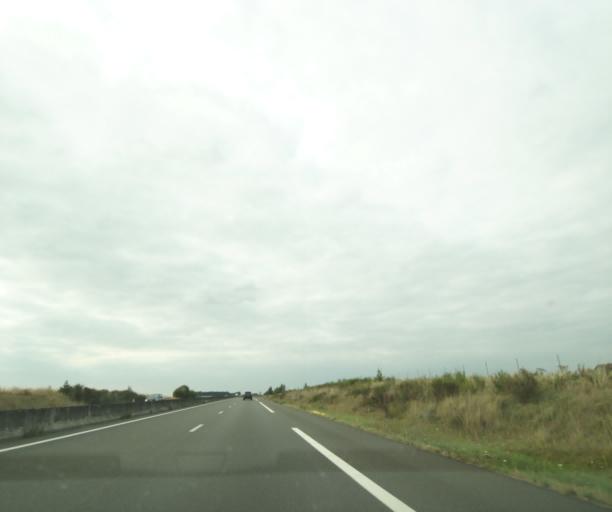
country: FR
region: Centre
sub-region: Departement d'Indre-et-Loire
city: Saint-Paterne-Racan
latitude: 47.6040
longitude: 0.5339
